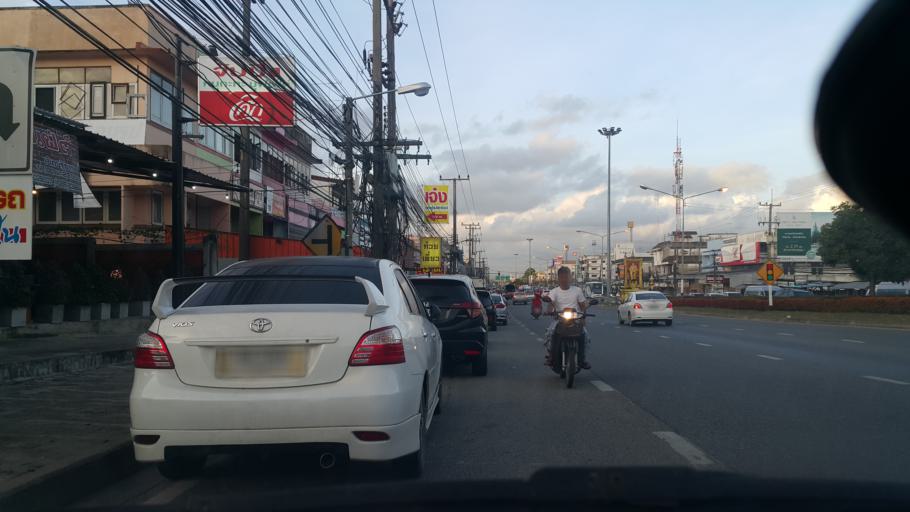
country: TH
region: Rayong
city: Ban Chang
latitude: 12.7219
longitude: 101.0490
